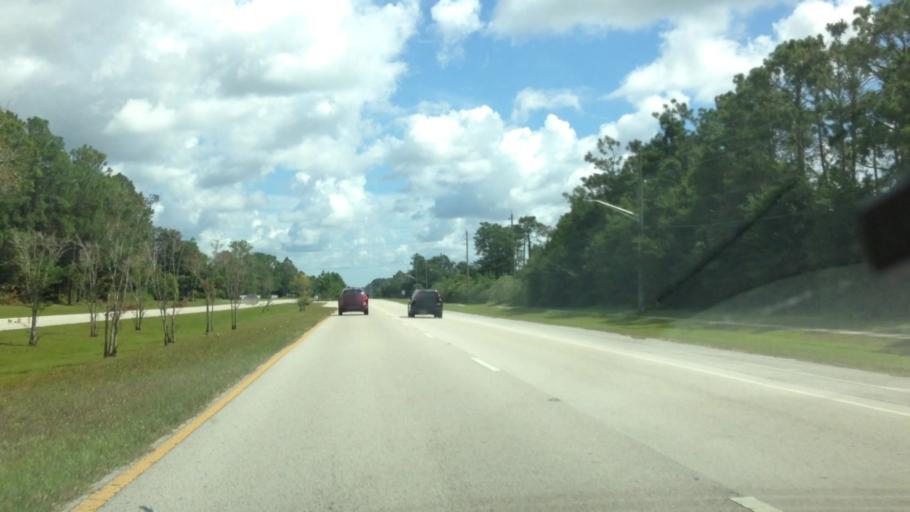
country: US
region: Florida
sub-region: Duval County
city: Jacksonville Beach
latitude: 30.2696
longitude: -81.4639
